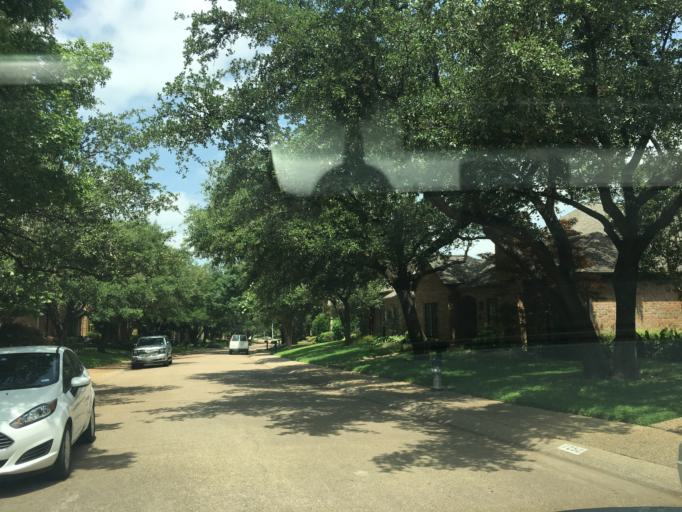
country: US
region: Texas
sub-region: Dallas County
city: University Park
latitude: 32.8714
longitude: -96.7792
